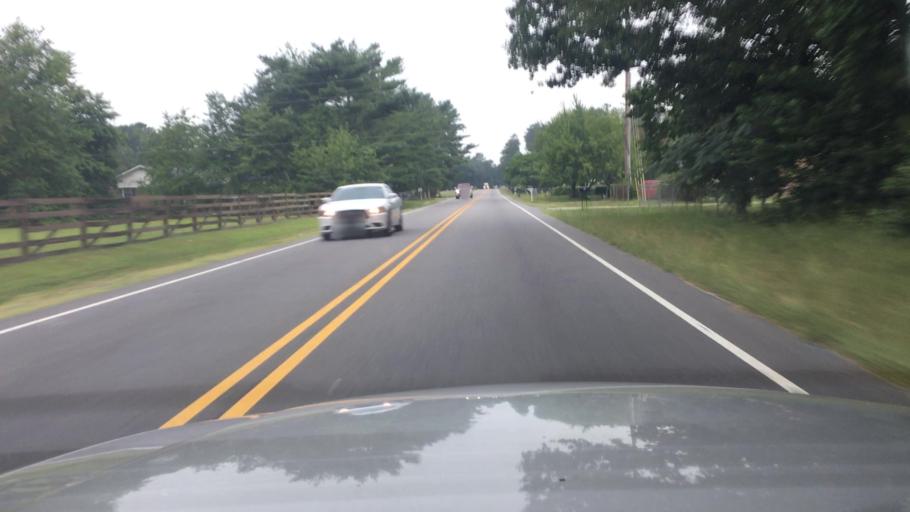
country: US
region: North Carolina
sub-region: Cumberland County
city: Hope Mills
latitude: 34.9765
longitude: -78.9896
